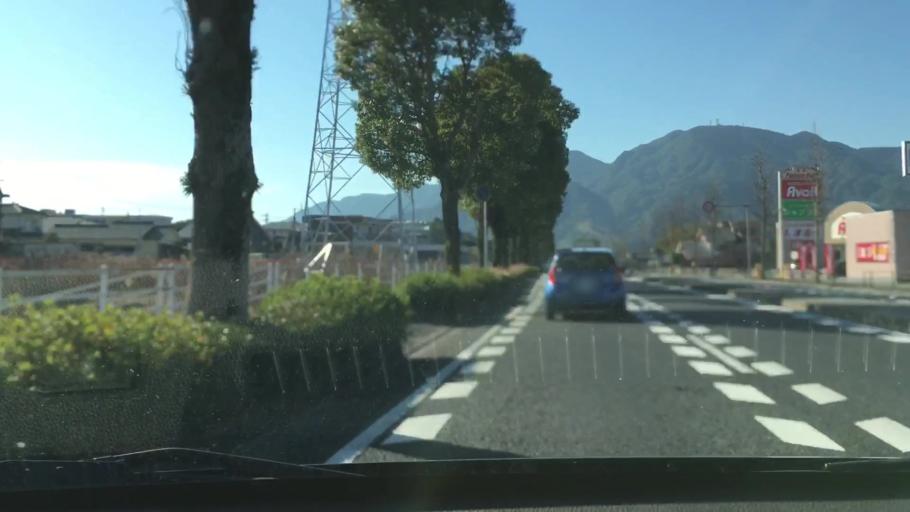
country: JP
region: Kagoshima
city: Kajiki
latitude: 31.7216
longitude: 130.6218
